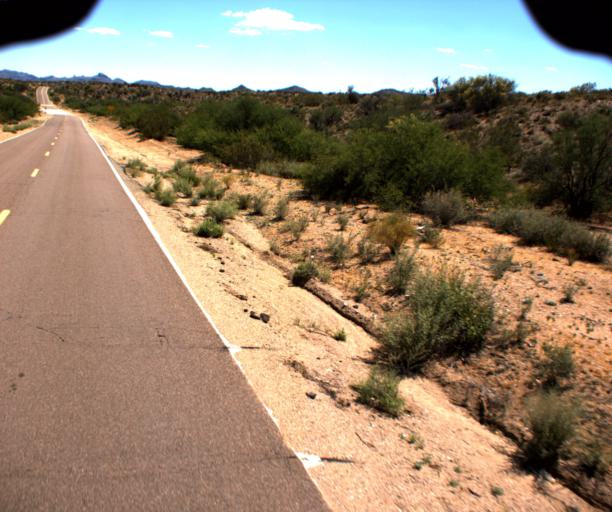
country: US
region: Arizona
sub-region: Yavapai County
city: Bagdad
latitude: 34.4453
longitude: -113.2424
